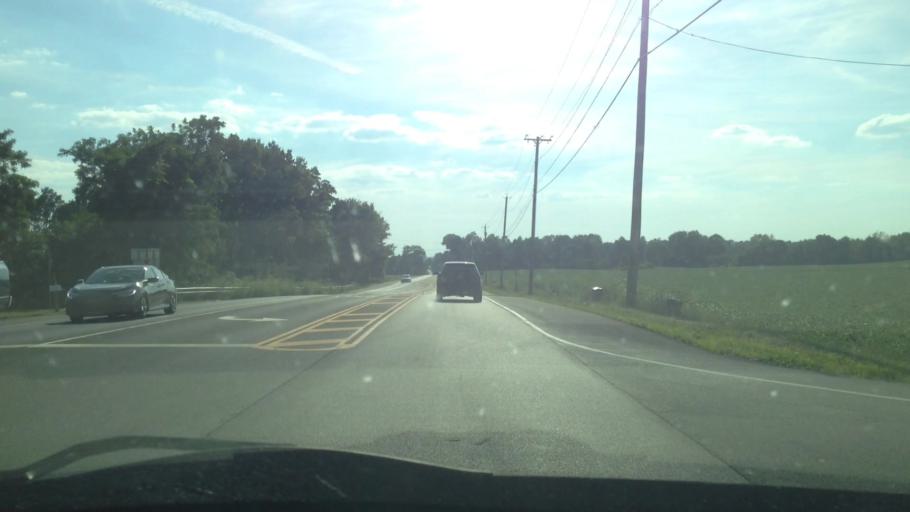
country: US
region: New York
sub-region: Onondaga County
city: Marcellus
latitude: 43.0347
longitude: -76.3653
